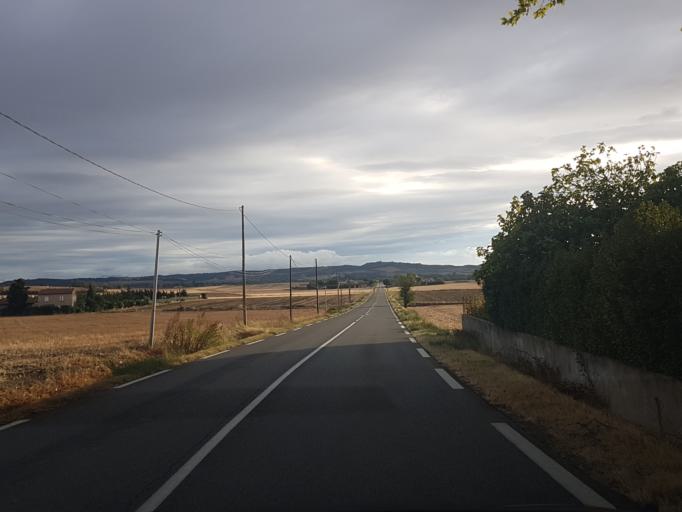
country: FR
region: Languedoc-Roussillon
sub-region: Departement de l'Aude
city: Bram
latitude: 43.2261
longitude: 2.0910
